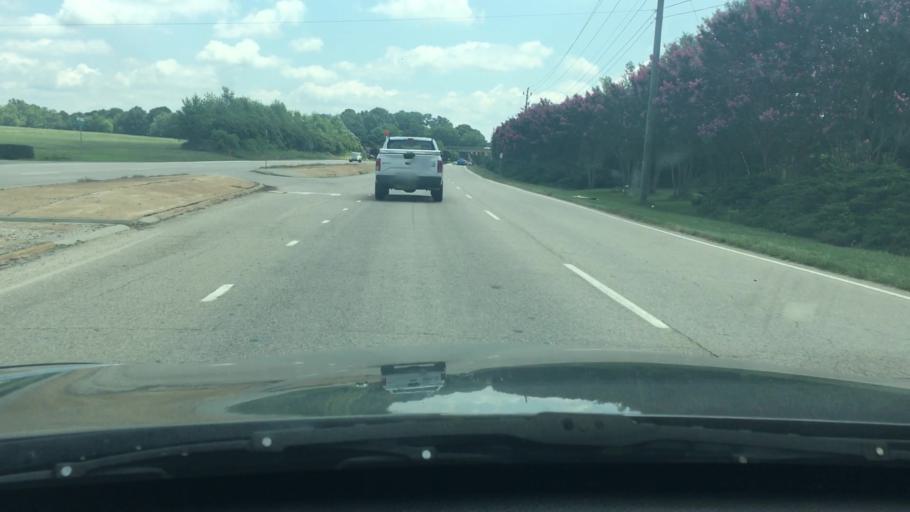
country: US
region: North Carolina
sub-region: Wake County
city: West Raleigh
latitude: 35.7957
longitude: -78.6999
